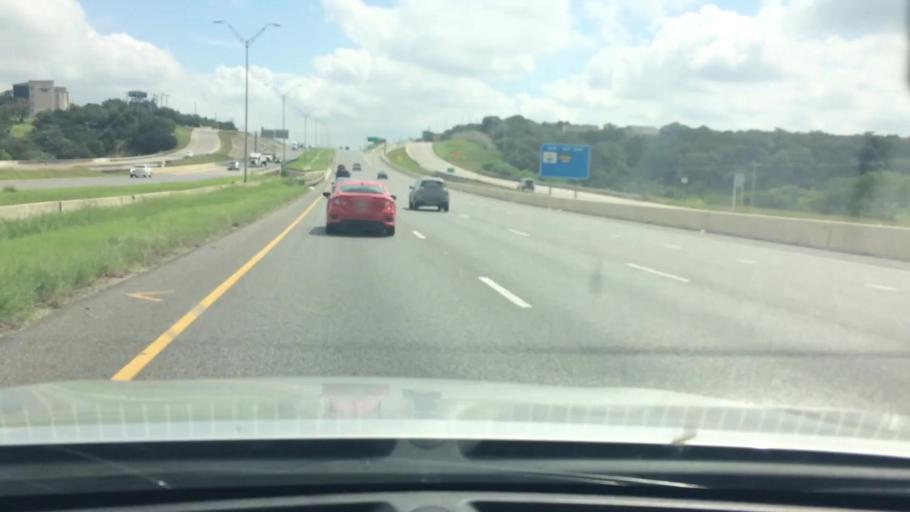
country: US
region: Texas
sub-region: Bexar County
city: Hollywood Park
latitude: 29.6045
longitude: -98.4520
